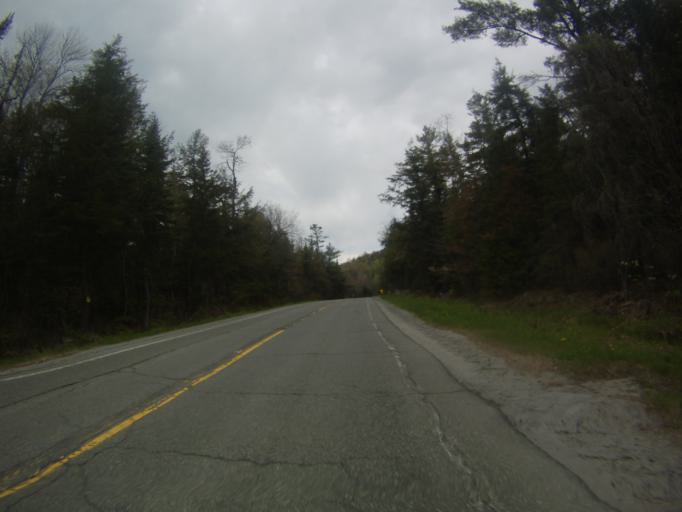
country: US
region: New York
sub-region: Essex County
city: Mineville
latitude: 44.0978
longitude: -73.5645
